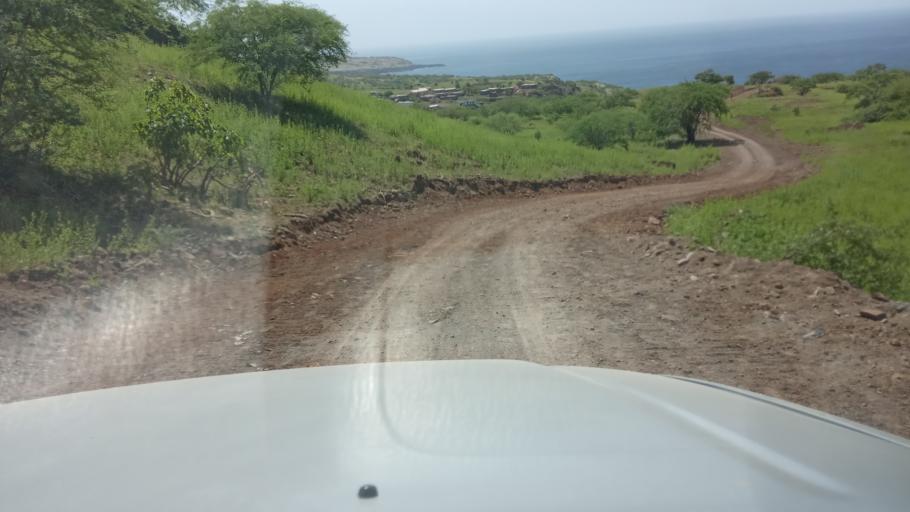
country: CV
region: Santa Catarina
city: Assomada
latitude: 15.1210
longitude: -23.7622
